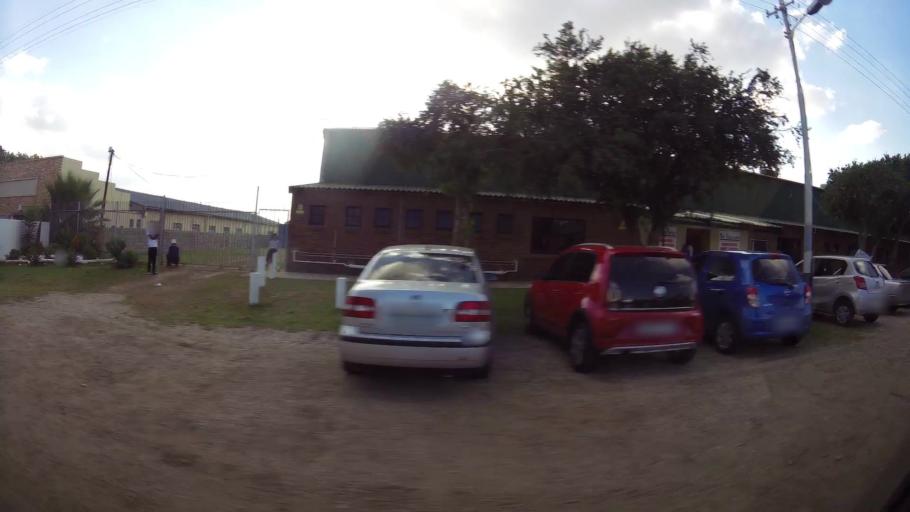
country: ZA
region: Eastern Cape
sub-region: Nelson Mandela Bay Metropolitan Municipality
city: Uitenhage
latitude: -33.7711
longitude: 25.3907
